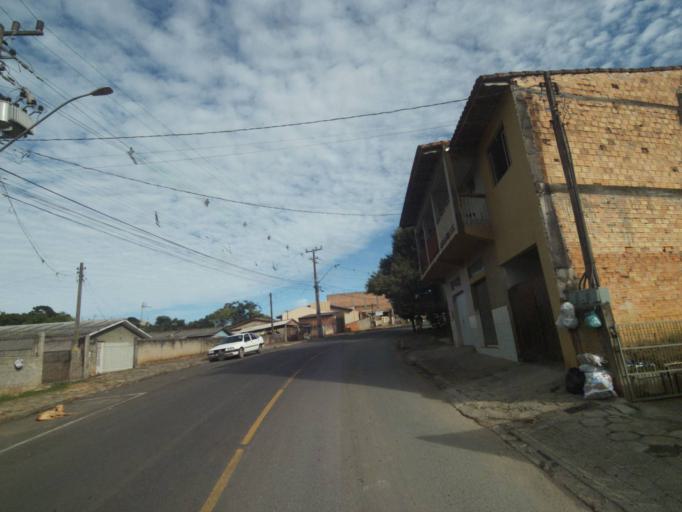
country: BR
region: Parana
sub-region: Telemaco Borba
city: Telemaco Borba
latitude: -24.3411
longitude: -50.6142
